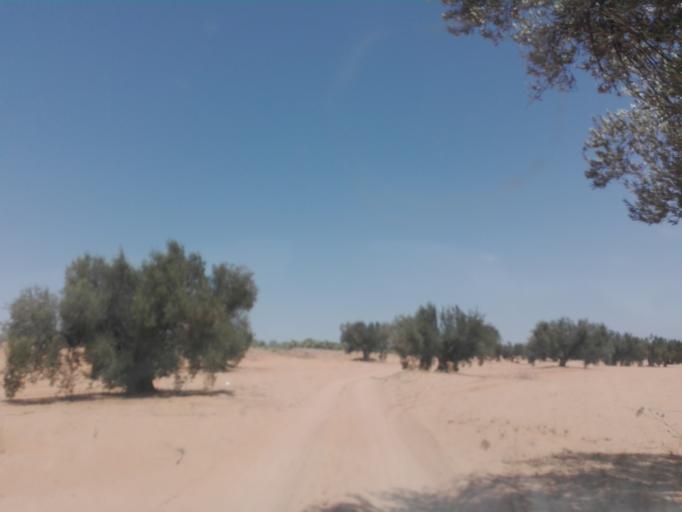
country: TN
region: Safaqis
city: Bi'r `Ali Bin Khalifah
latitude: 34.6490
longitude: 10.2774
